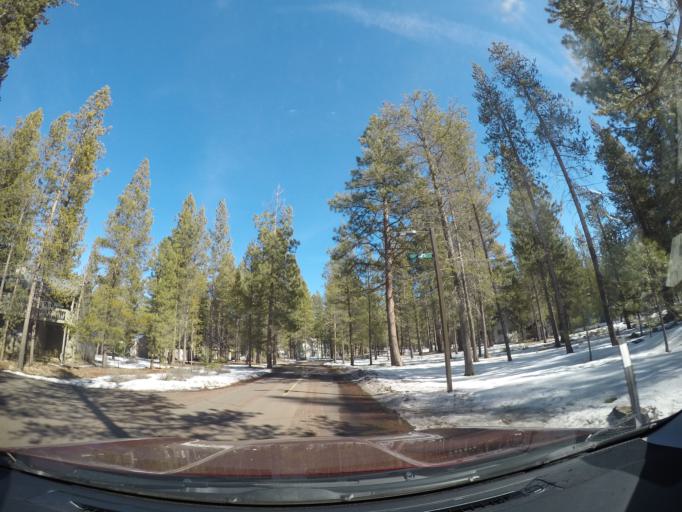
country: US
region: Oregon
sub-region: Deschutes County
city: Sunriver
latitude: 43.8716
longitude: -121.4336
